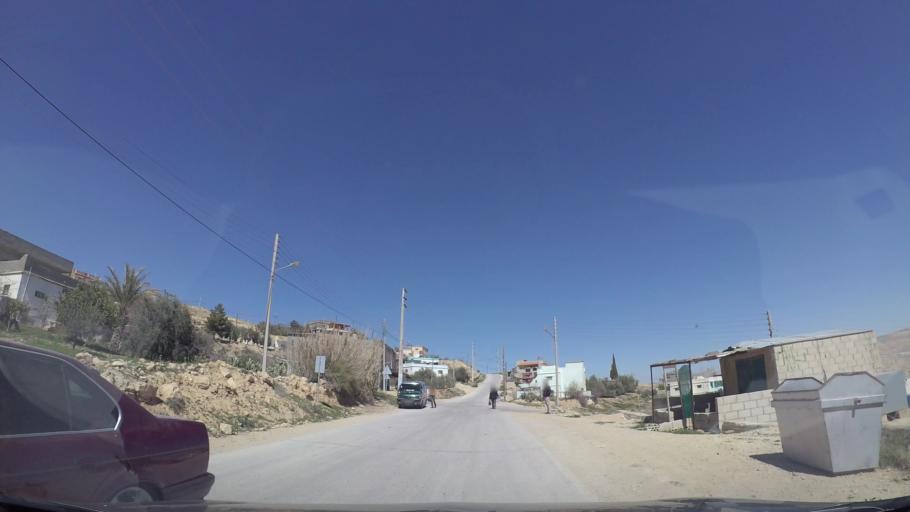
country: JO
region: Tafielah
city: At Tafilah
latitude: 30.8358
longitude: 35.5752
